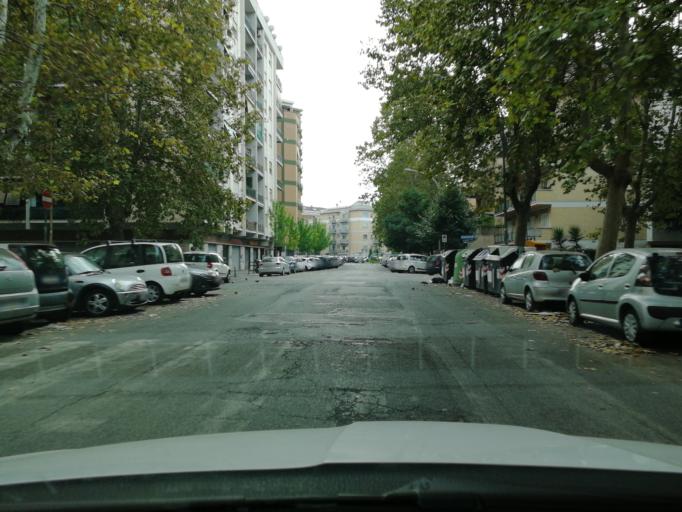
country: IT
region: Latium
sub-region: Citta metropolitana di Roma Capitale
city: Rome
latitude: 41.8634
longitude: 12.5470
